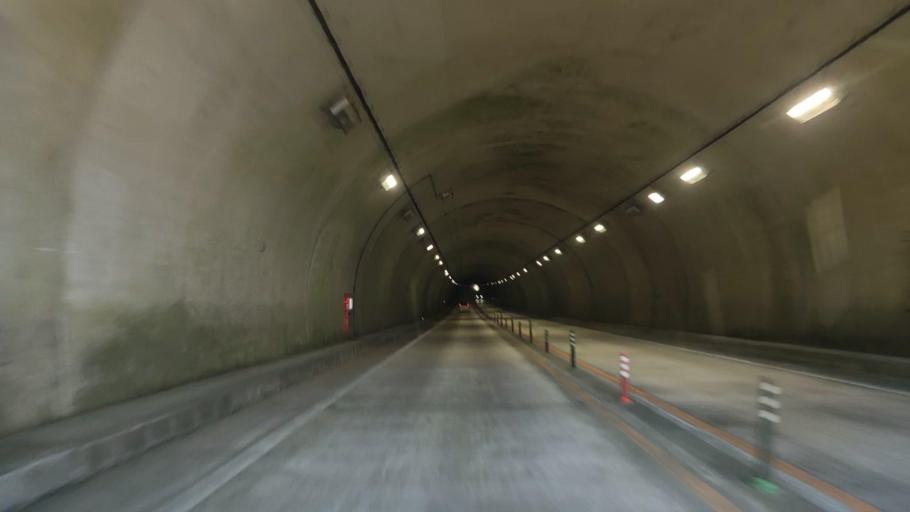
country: JP
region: Wakayama
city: Shingu
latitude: 33.6081
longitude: 135.9166
